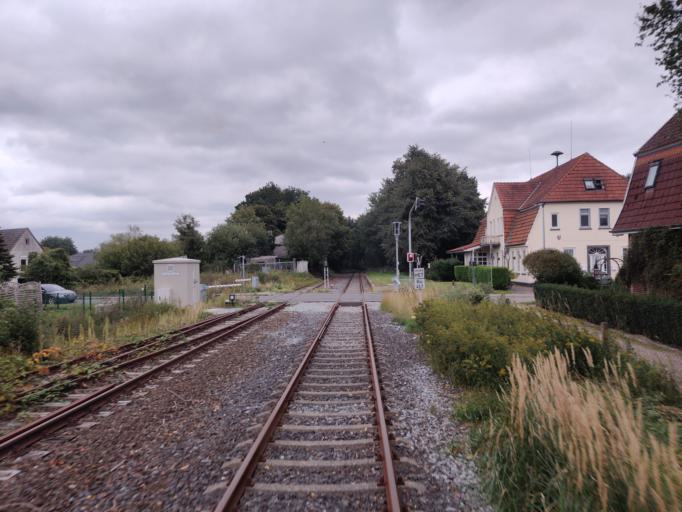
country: DE
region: Lower Saxony
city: Osterholz-Scharmbeck
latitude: 53.2336
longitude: 8.8173
